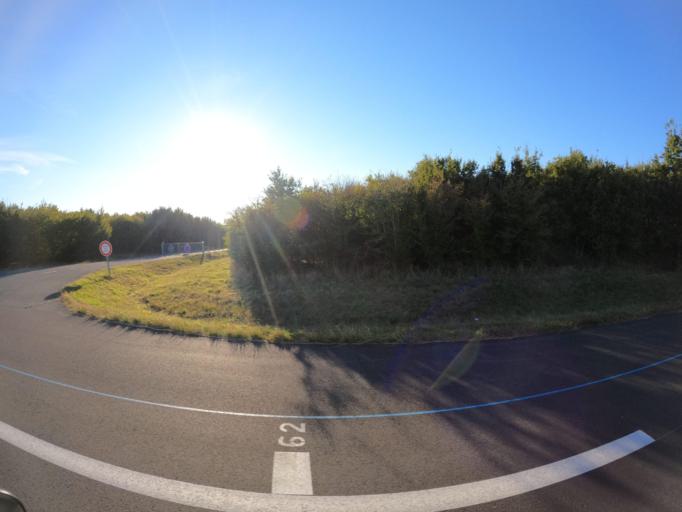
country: FR
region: Pays de la Loire
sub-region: Departement de la Vendee
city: Saint-Laurent-sur-Sevre
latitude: 46.9792
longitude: -0.9179
